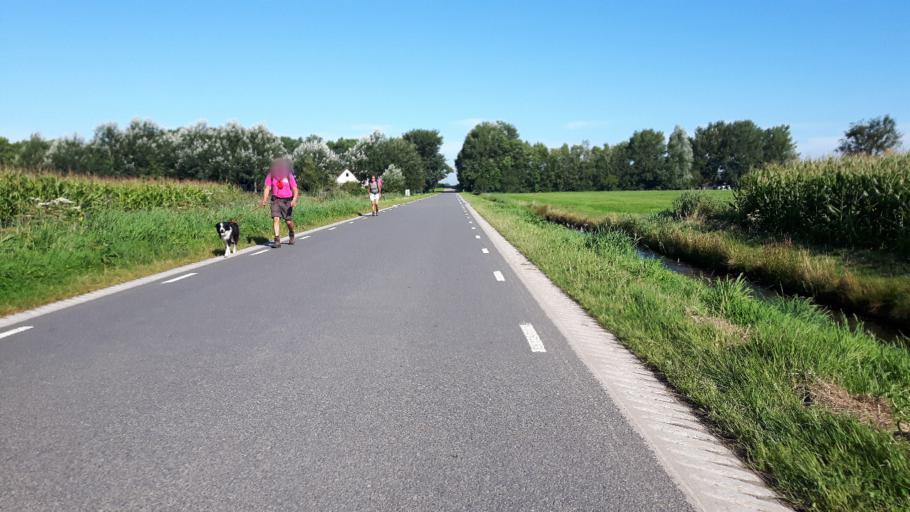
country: NL
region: Overijssel
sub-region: Gemeente Steenwijkerland
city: Oldemarkt
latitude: 52.8110
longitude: 5.9111
